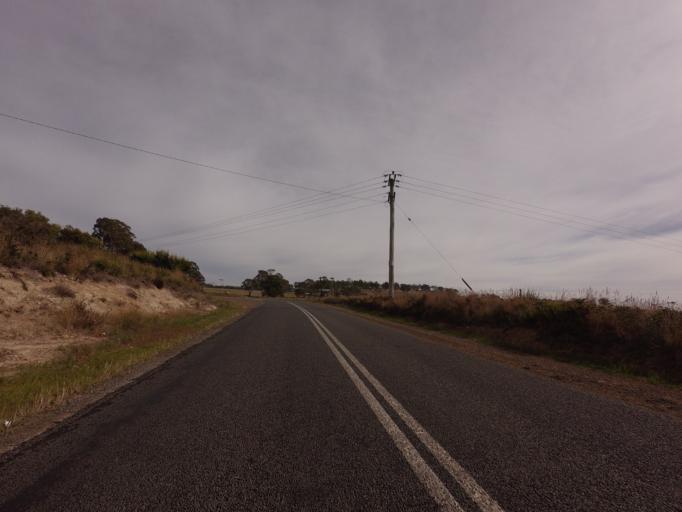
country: AU
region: Tasmania
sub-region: Brighton
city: Bridgewater
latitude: -42.3881
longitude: 147.4238
